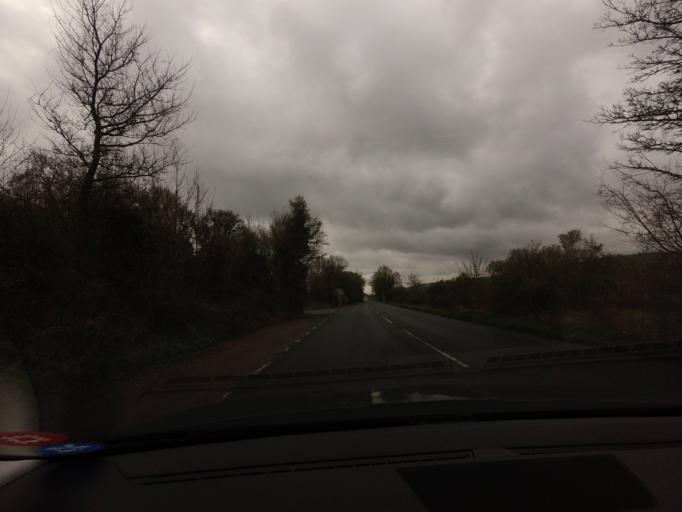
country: GB
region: England
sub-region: Kent
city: Shoreham
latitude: 51.3404
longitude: 0.1930
